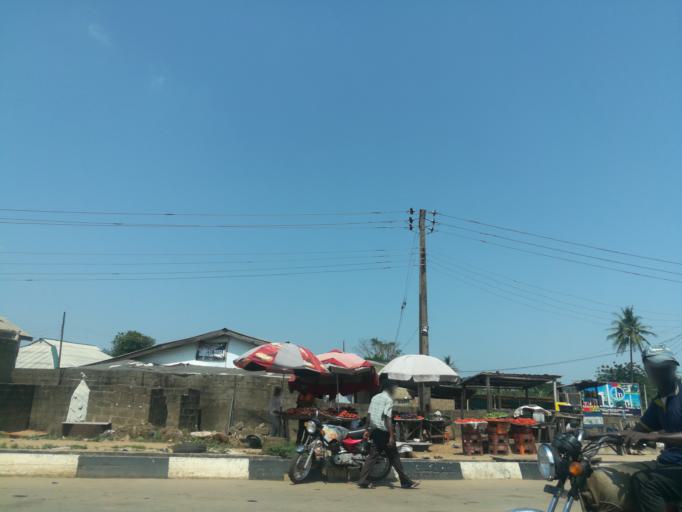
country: NG
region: Ogun
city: Abeokuta
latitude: 7.1489
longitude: 3.3590
